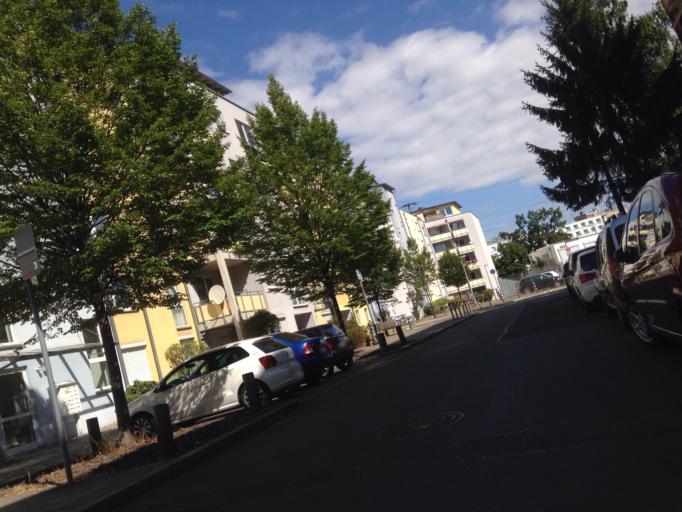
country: DE
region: Bavaria
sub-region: Regierungsbezirk Mittelfranken
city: Nuernberg
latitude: 49.4447
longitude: 11.0877
